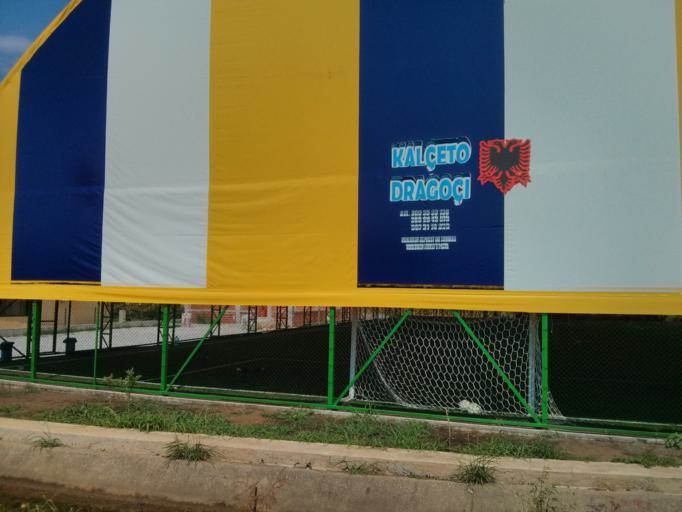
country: AL
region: Shkoder
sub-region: Rrethi i Malesia e Madhe
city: Gruemire
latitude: 42.1204
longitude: 19.5657
